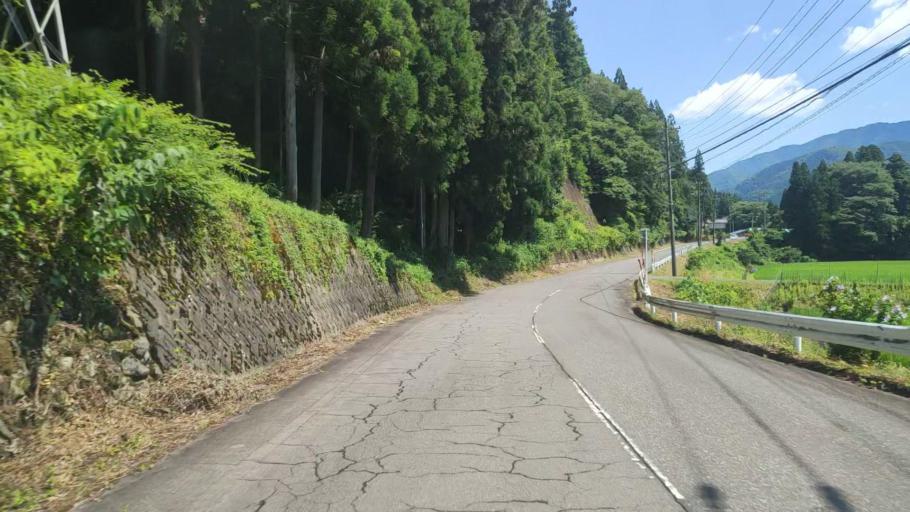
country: JP
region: Gifu
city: Godo
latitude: 35.6736
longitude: 136.5757
